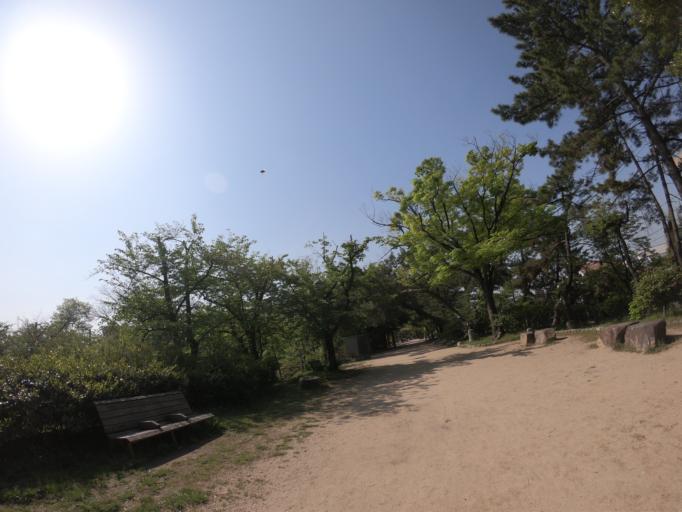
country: JP
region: Hyogo
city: Nishinomiya-hama
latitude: 34.7329
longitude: 135.3289
